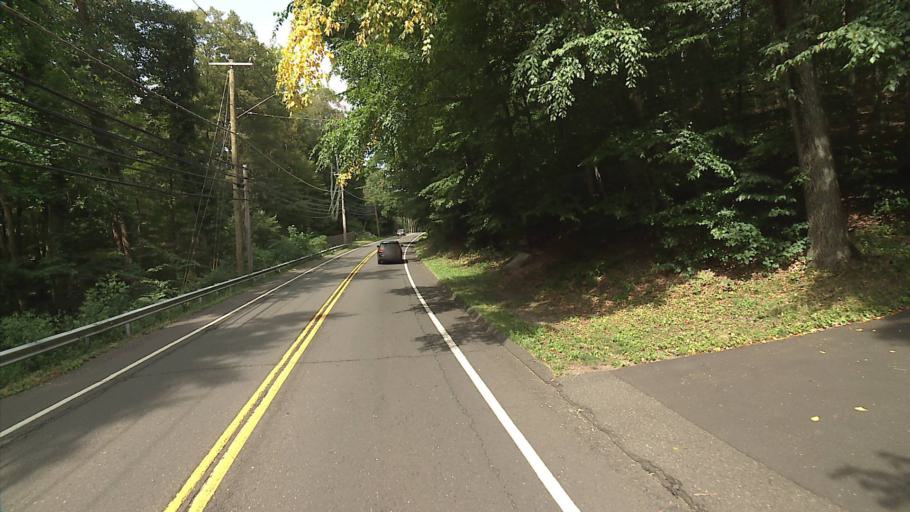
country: US
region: Connecticut
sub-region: Fairfield County
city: North Stamford
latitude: 41.1081
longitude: -73.5696
